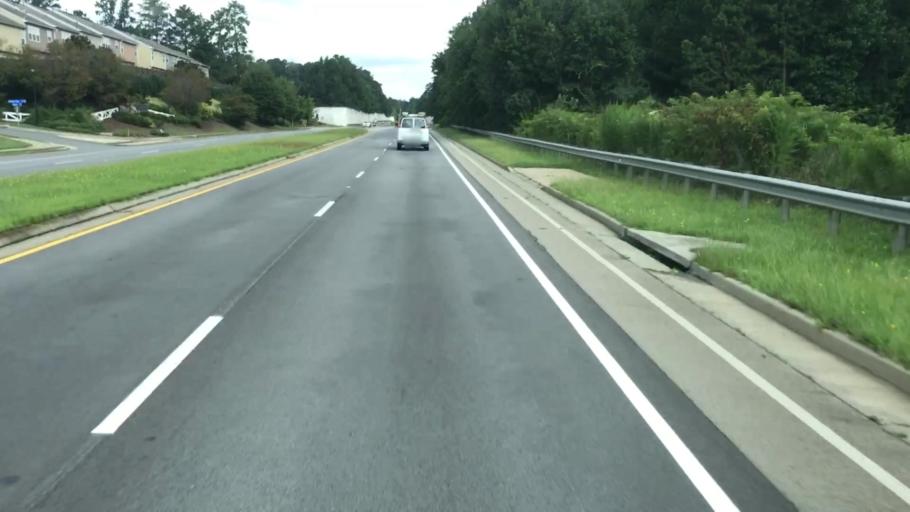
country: US
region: Georgia
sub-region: Gwinnett County
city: Duluth
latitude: 33.9687
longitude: -84.0698
